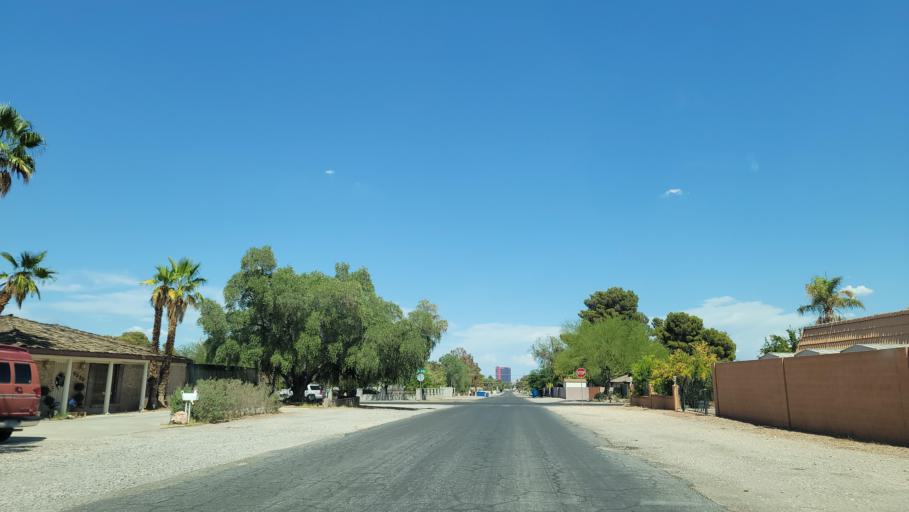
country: US
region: Nevada
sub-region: Clark County
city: Spring Valley
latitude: 36.1349
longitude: -115.2347
